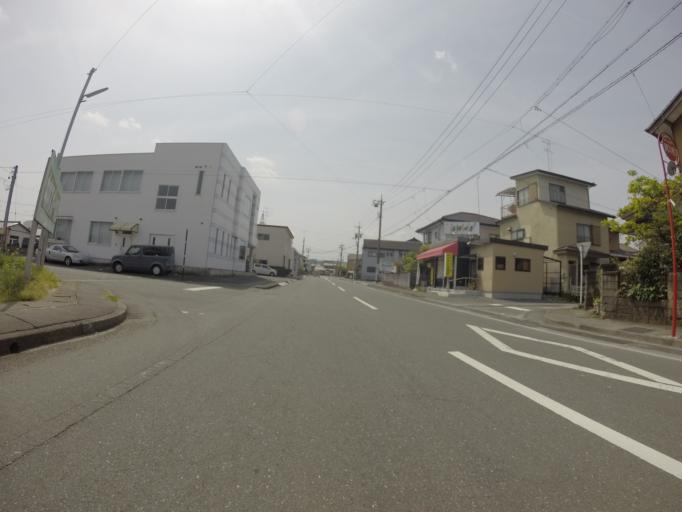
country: JP
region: Shizuoka
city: Kakegawa
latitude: 34.7725
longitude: 138.0032
